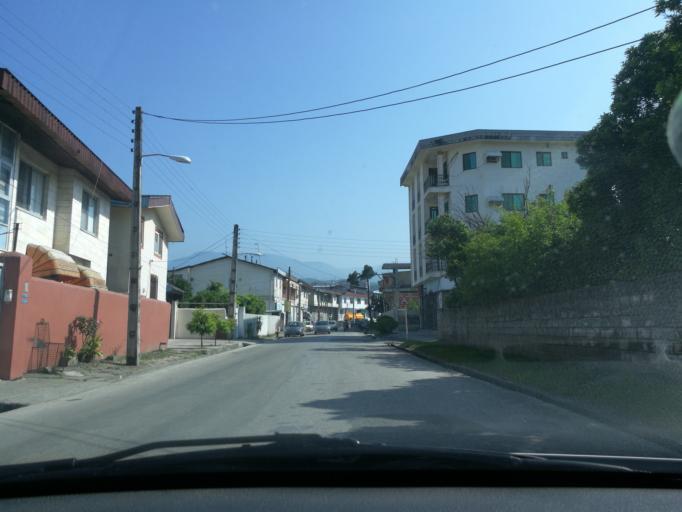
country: IR
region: Mazandaran
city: Chalus
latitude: 36.6587
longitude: 51.4259
